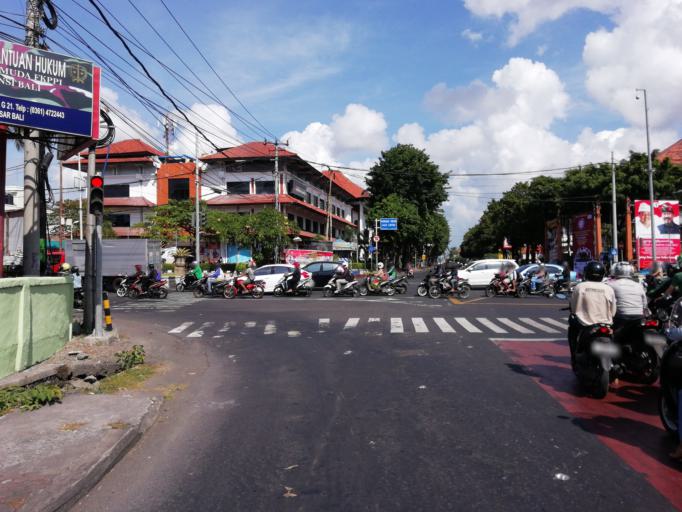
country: ID
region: Bali
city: Denpasar
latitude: -8.6698
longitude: 115.2184
